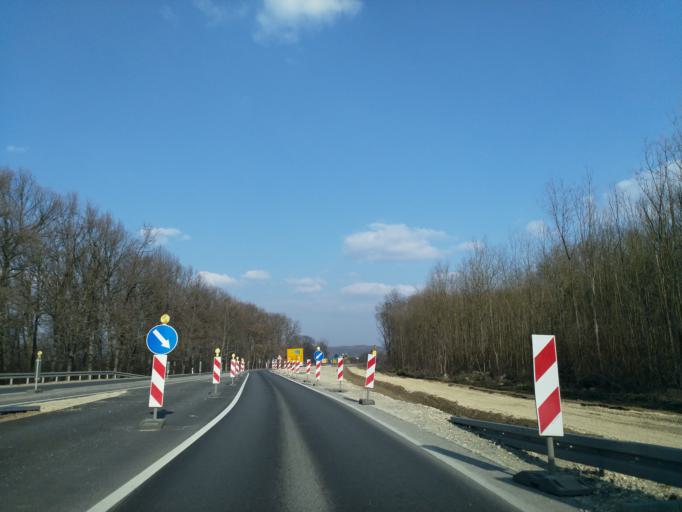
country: RS
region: Central Serbia
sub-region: Sumadijski Okrug
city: Batocina
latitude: 44.1470
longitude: 21.1030
